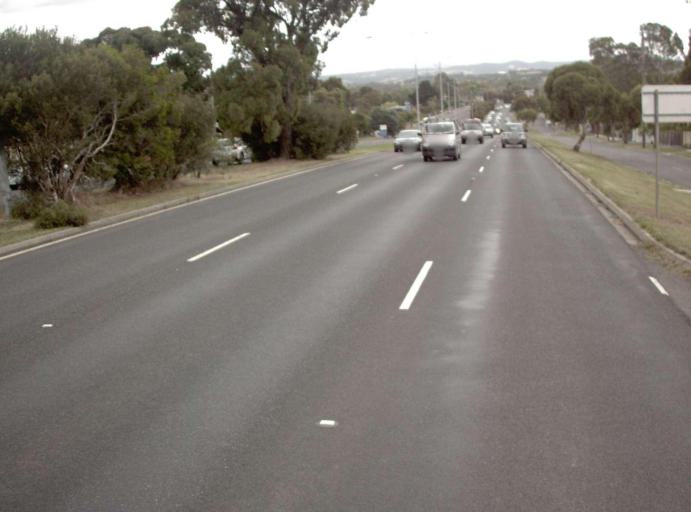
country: AU
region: Victoria
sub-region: Maroondah
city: Croydon North
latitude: -37.7776
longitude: 145.2924
